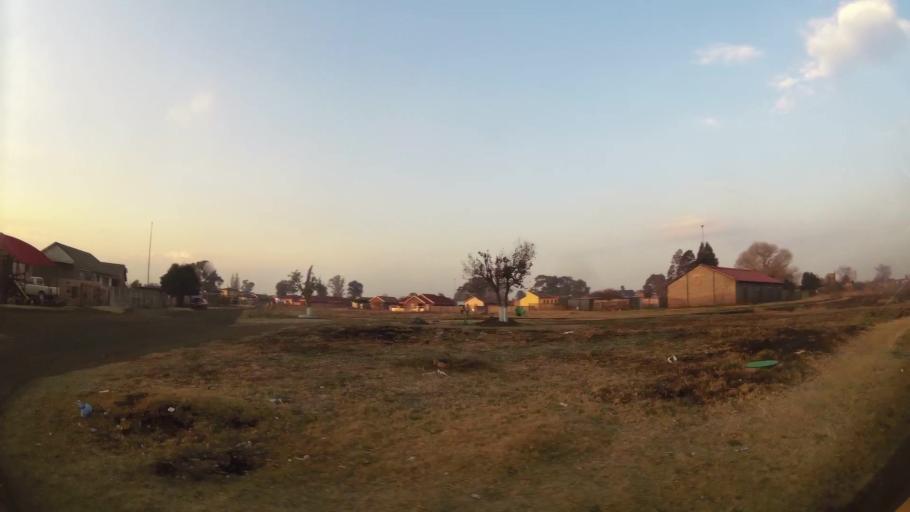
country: ZA
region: Gauteng
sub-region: City of Johannesburg Metropolitan Municipality
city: Orange Farm
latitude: -26.5408
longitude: 27.8828
